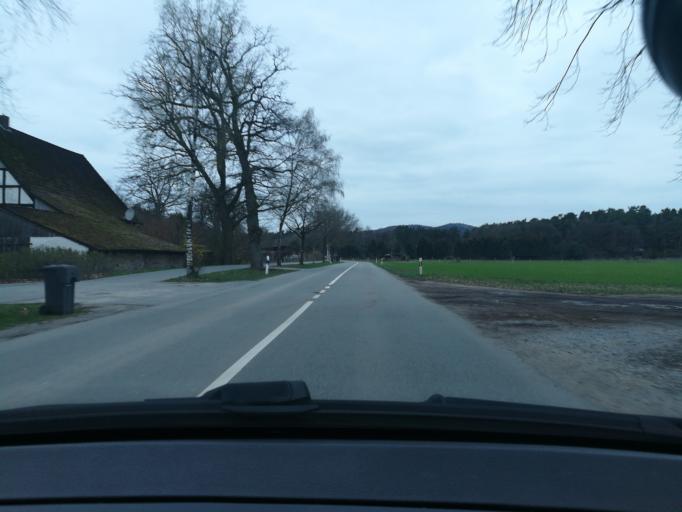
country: DE
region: North Rhine-Westphalia
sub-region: Regierungsbezirk Detmold
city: Oerlinghausen
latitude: 51.9457
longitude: 8.6385
